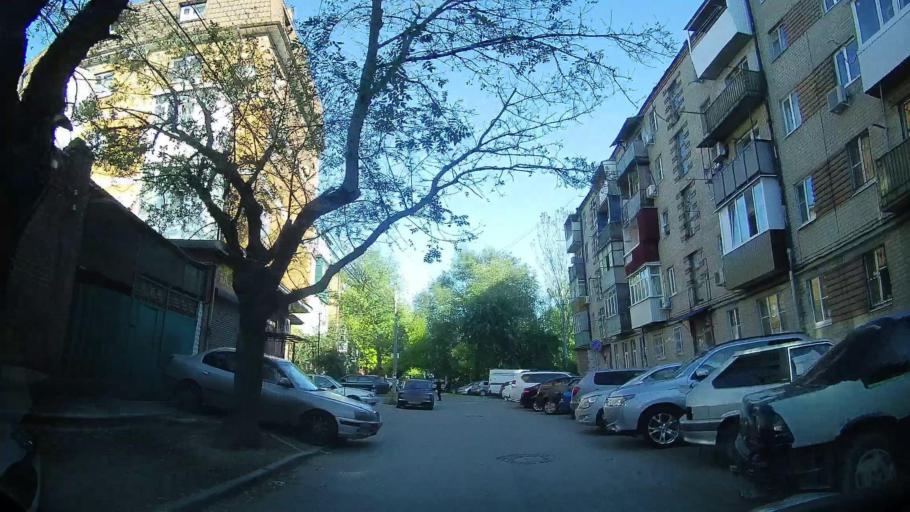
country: RU
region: Rostov
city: Rostov-na-Donu
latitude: 47.2119
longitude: 39.6837
